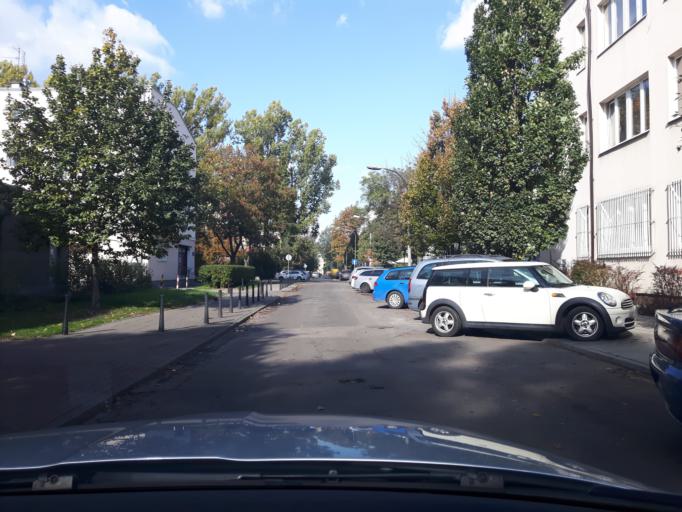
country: PL
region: Masovian Voivodeship
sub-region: Warszawa
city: Praga Poludnie
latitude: 52.2360
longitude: 21.0635
